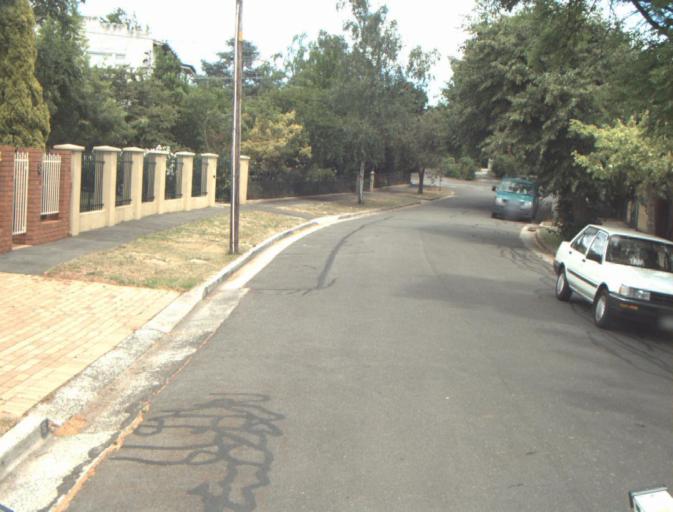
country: AU
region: Tasmania
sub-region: Launceston
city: Newstead
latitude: -41.4442
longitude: 147.1634
